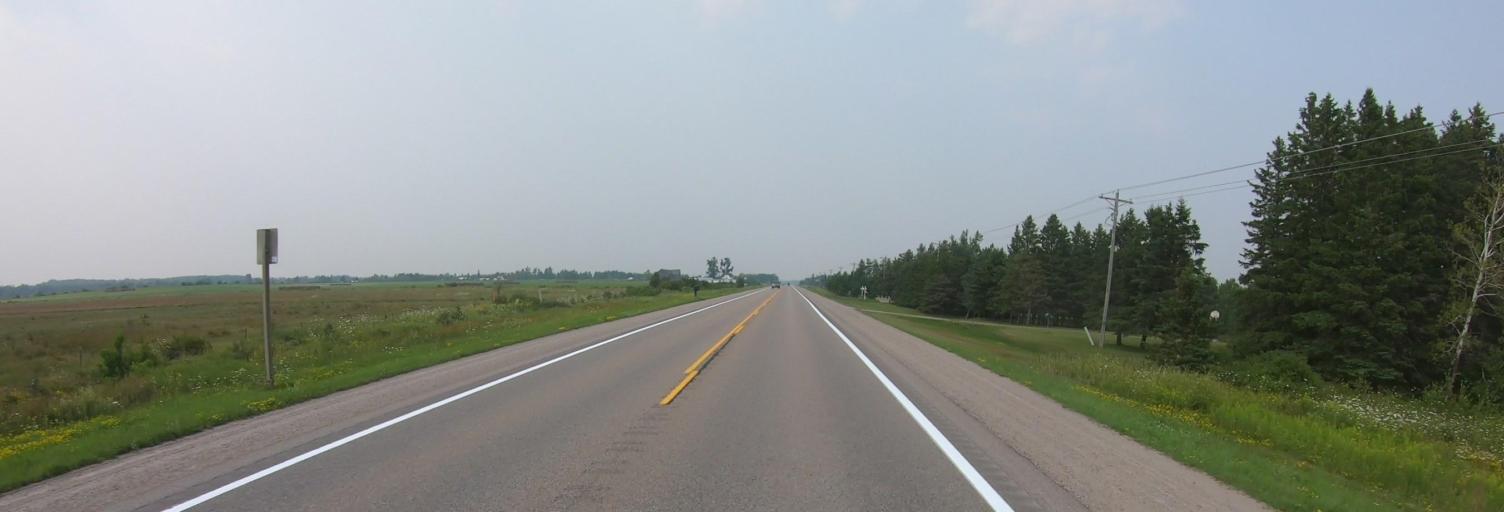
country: US
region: Michigan
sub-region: Chippewa County
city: Sault Ste. Marie
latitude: 46.3374
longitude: -84.3638
